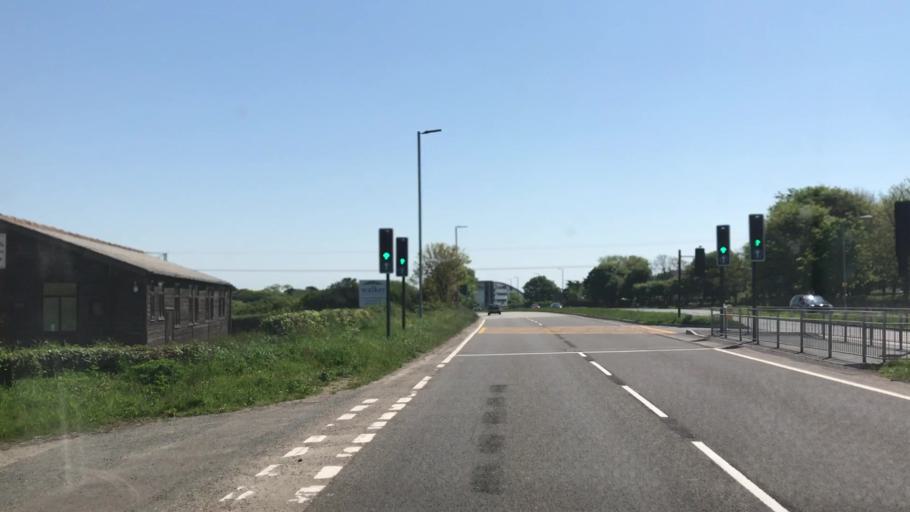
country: GB
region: England
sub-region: Cornwall
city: Truro
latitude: 50.2640
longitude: -5.1096
